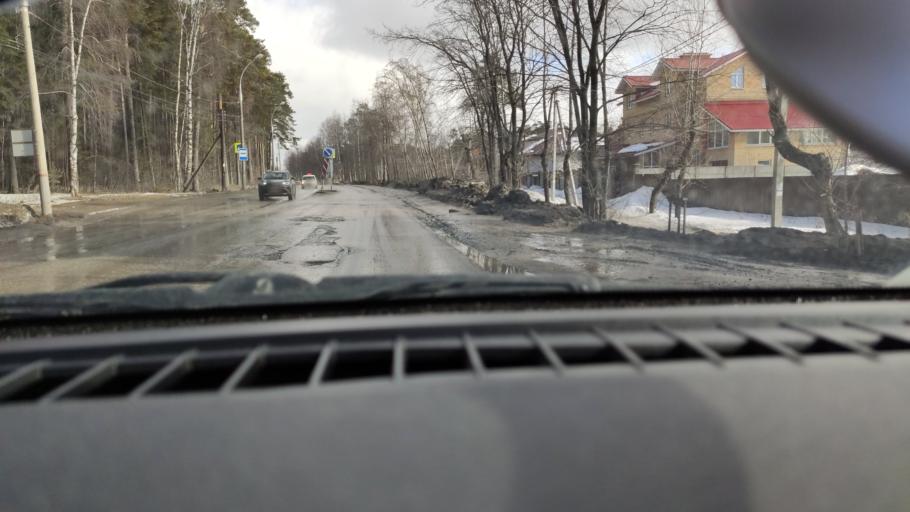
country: RU
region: Perm
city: Kondratovo
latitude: 58.0120
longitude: 55.9888
